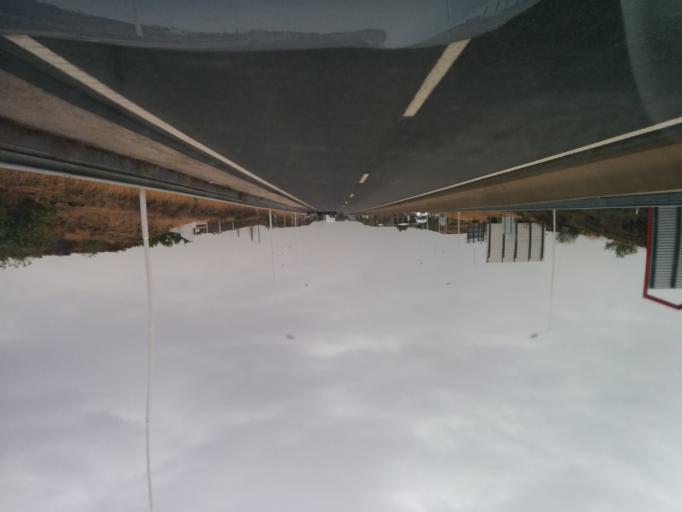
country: PT
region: Faro
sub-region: Castro Marim
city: Castro Marim
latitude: 37.2356
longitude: -7.4411
